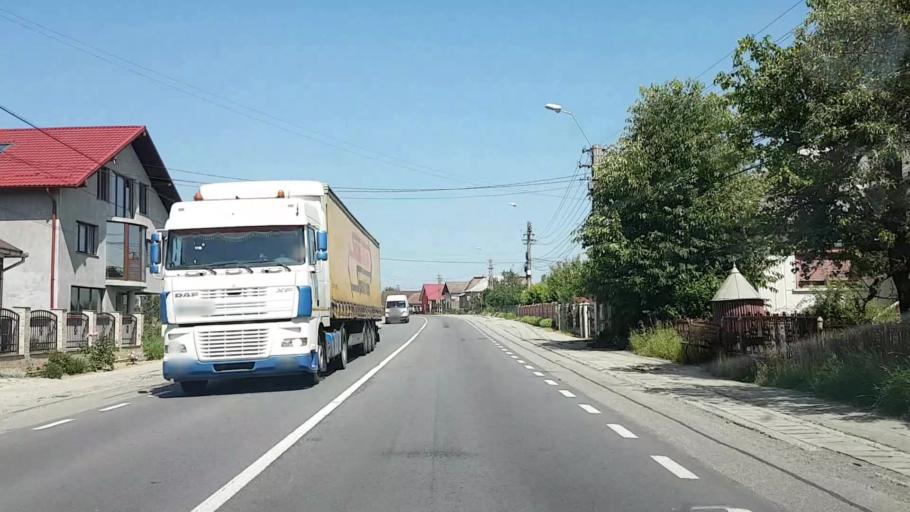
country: RO
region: Cluj
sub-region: Comuna Cusdrioara
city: Cusdrioara
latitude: 47.1707
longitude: 23.9215
